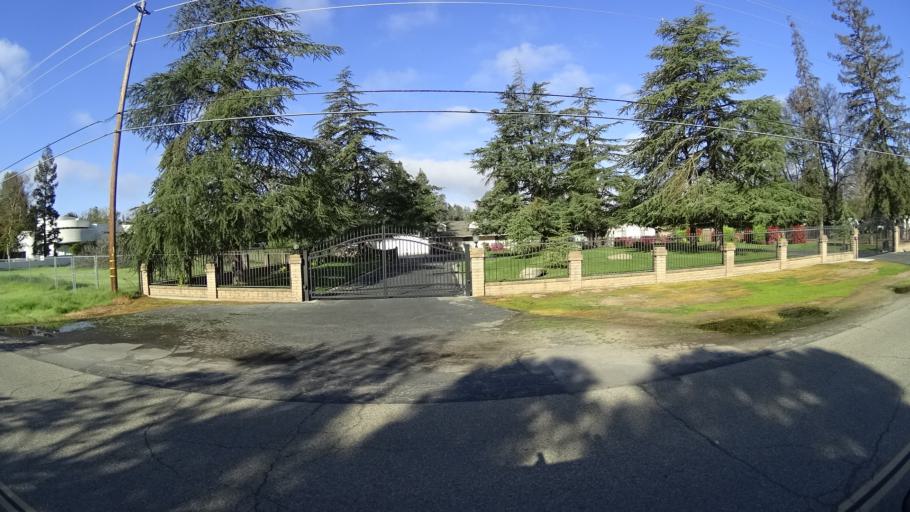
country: US
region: California
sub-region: Fresno County
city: Fresno
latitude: 36.8265
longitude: -119.8308
